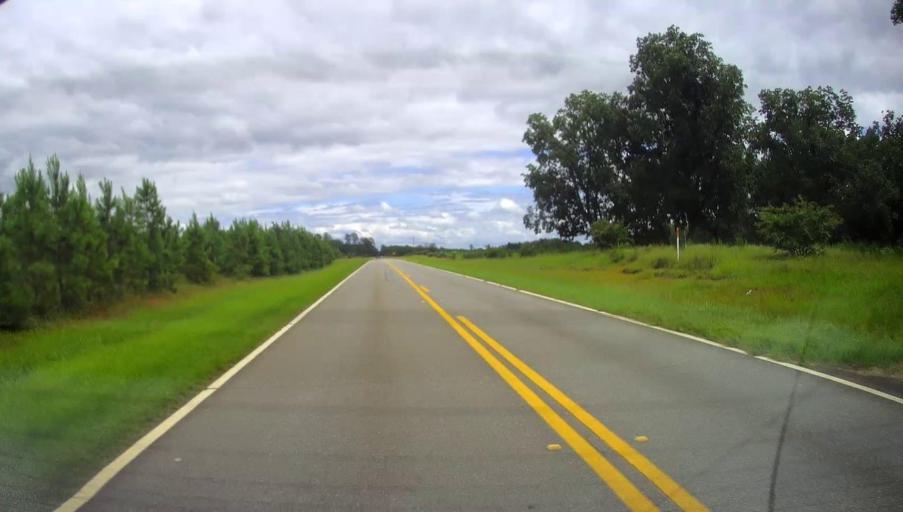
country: US
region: Georgia
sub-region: Twiggs County
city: Jeffersonville
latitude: 32.6802
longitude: -83.3126
